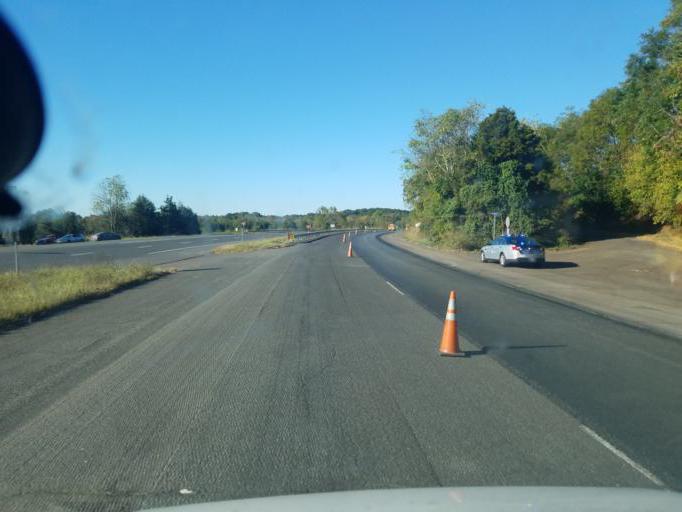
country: US
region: Virginia
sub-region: Fauquier County
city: Bealeton
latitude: 38.5270
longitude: -77.8217
